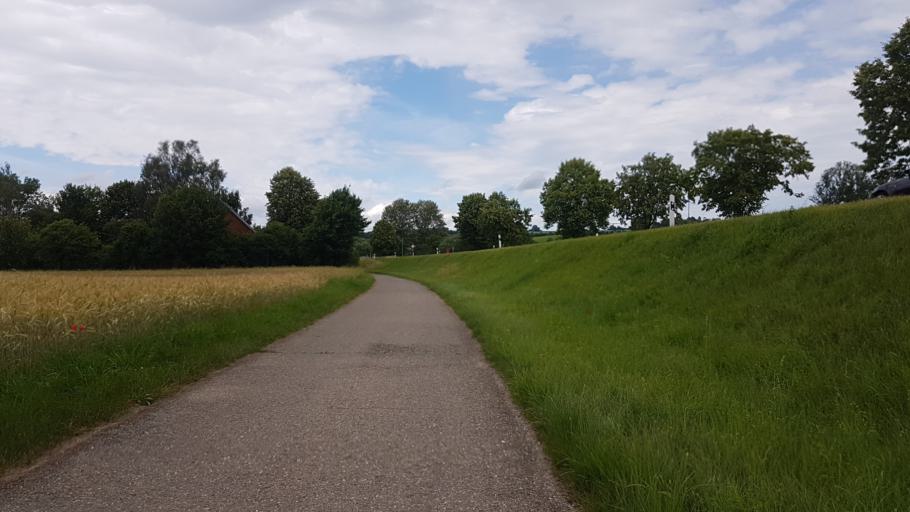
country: DE
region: Baden-Wuerttemberg
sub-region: Tuebingen Region
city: Mengen
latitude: 48.0608
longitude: 9.3463
